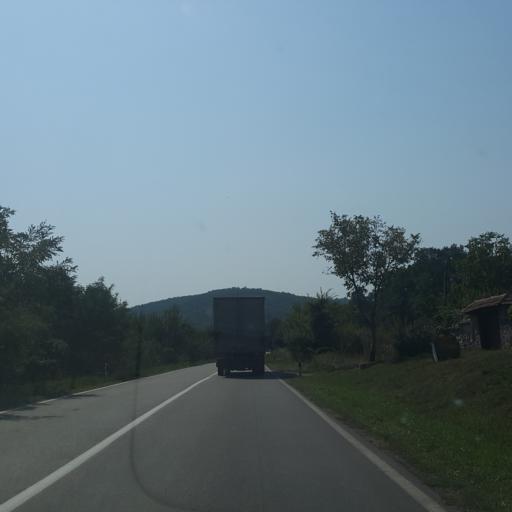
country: RS
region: Central Serbia
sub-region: Zajecarski Okrug
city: Zajecar
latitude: 43.8213
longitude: 22.2875
